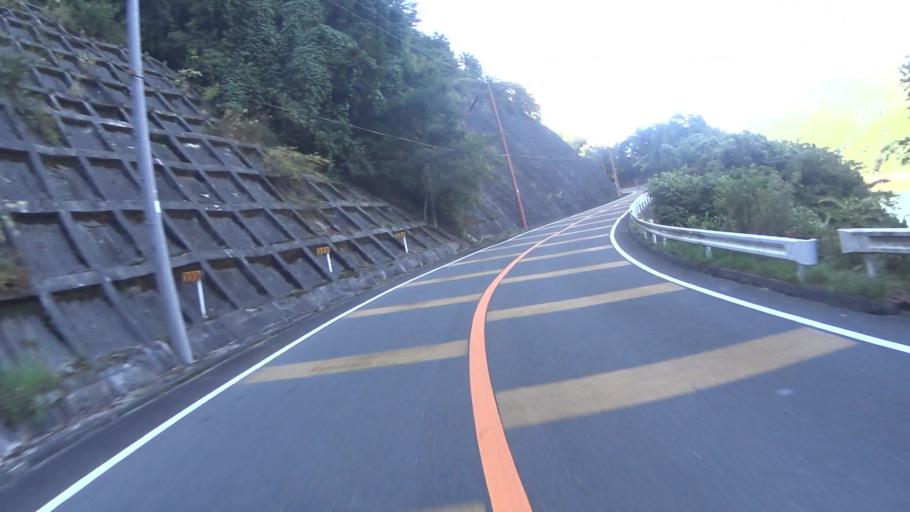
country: JP
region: Kyoto
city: Kameoka
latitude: 35.1302
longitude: 135.5408
